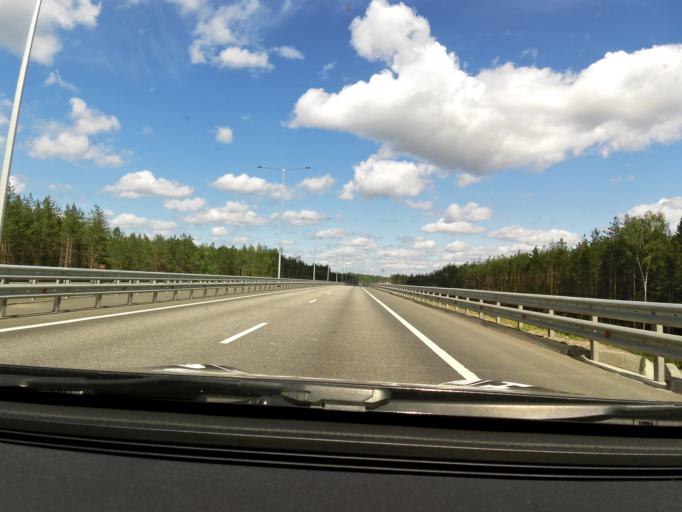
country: RU
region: Tverskaya
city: Krasnomayskiy
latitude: 57.6330
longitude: 34.2379
